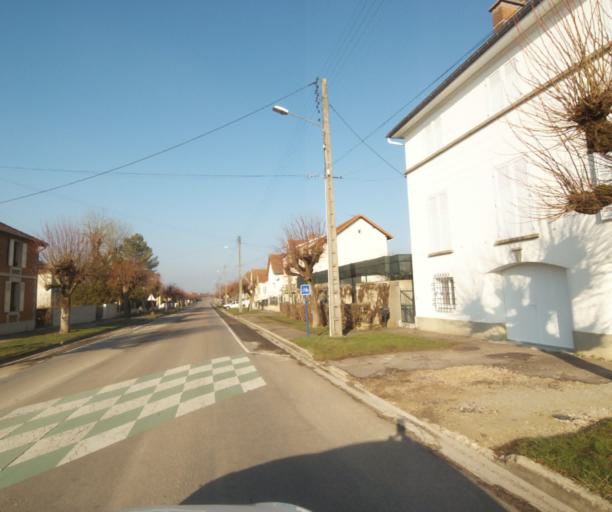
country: FR
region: Champagne-Ardenne
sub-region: Departement de la Haute-Marne
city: Montier-en-Der
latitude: 48.4808
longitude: 4.7675
